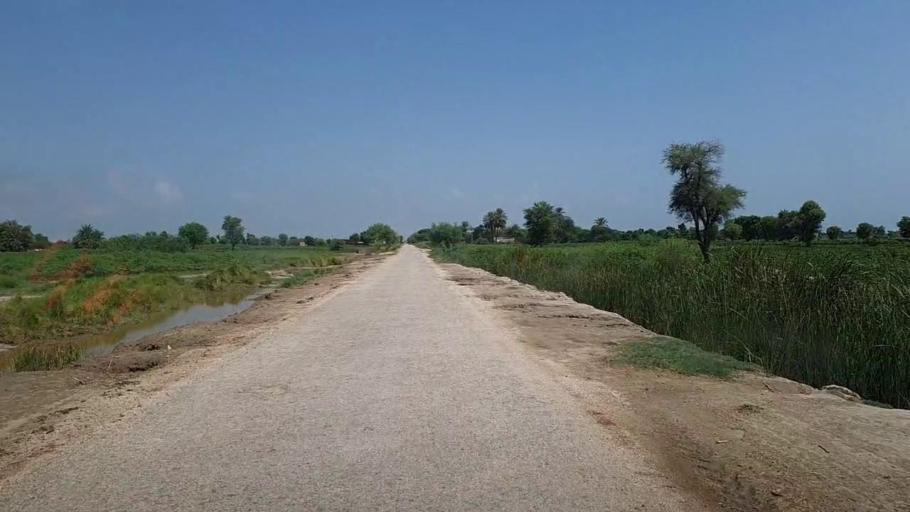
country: PK
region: Sindh
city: Bhiria
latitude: 26.8891
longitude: 68.2298
